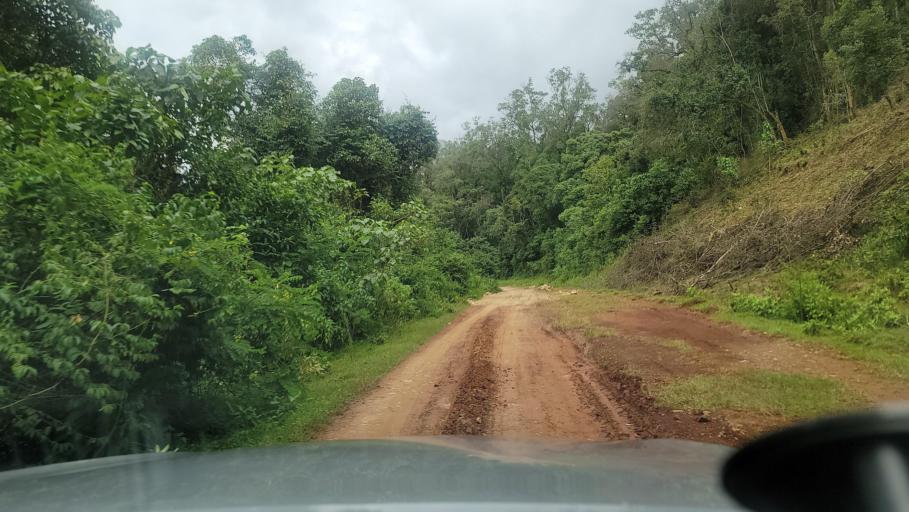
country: ET
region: Southern Nations, Nationalities, and People's Region
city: Bonga
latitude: 7.6272
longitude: 36.2140
